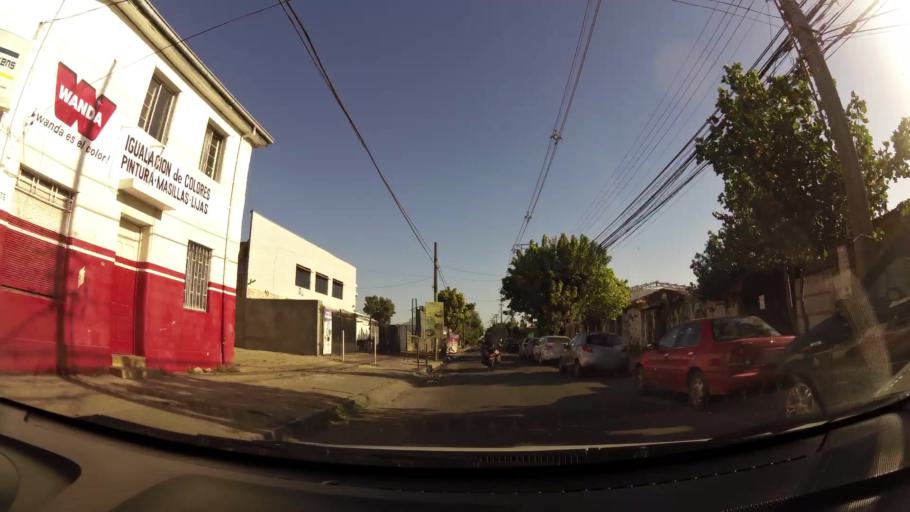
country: CL
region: Maule
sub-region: Provincia de Talca
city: Talca
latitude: -35.4303
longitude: -71.6542
